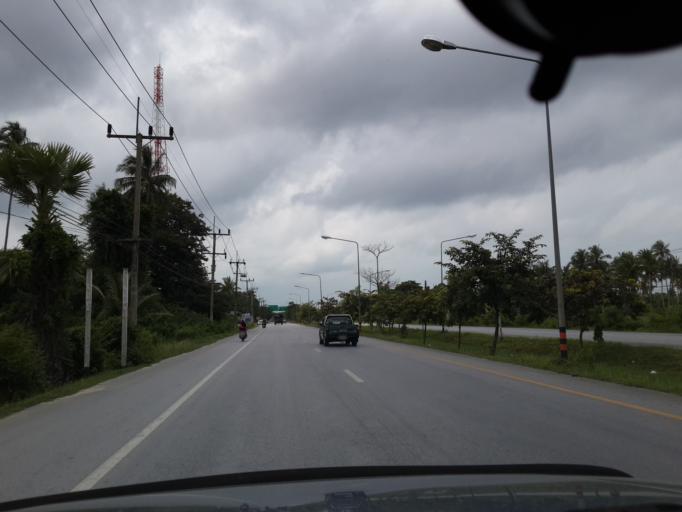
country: TH
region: Pattani
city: Pattani
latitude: 6.8712
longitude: 101.2870
